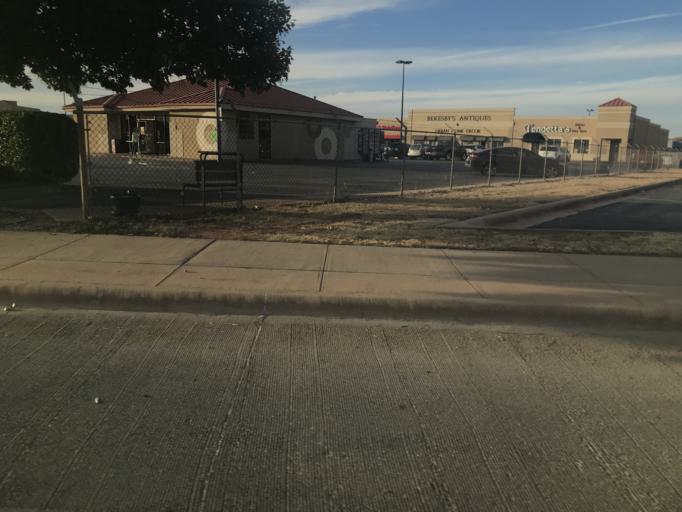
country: US
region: Texas
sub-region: Taylor County
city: Abilene
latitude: 32.4310
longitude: -99.7818
